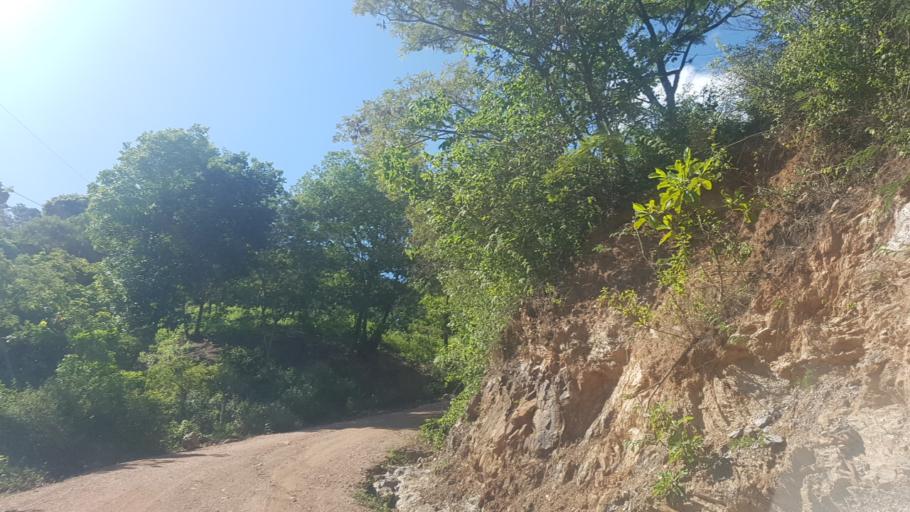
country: NI
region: Nueva Segovia
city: Ocotal
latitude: 13.6416
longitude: -86.6202
